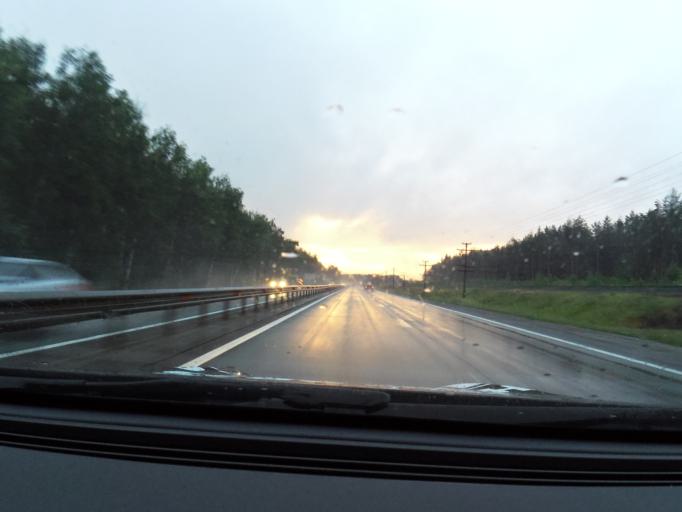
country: RU
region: Tatarstan
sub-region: Tukayevskiy Rayon
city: Naberezhnyye Chelny
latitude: 55.7453
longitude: 52.2460
